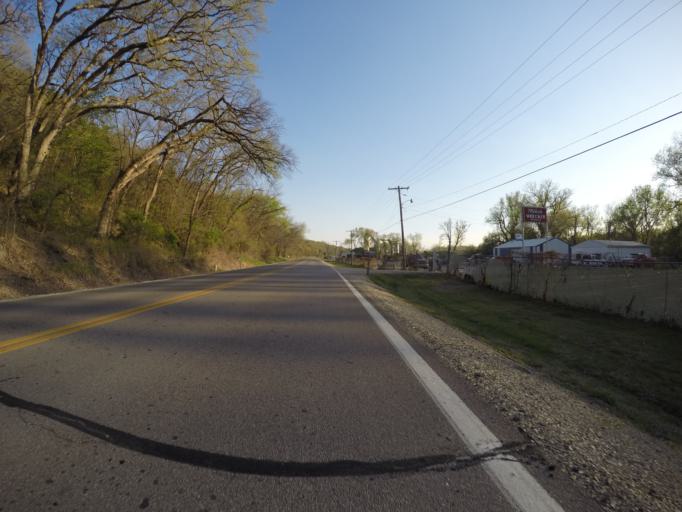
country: US
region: Kansas
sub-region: Riley County
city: Manhattan
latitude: 39.1704
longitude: -96.5533
